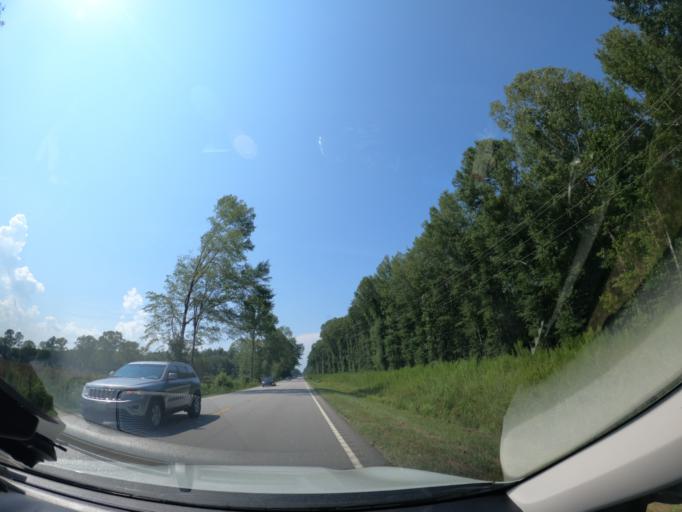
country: US
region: South Carolina
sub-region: Richland County
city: Hopkins
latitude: 33.8822
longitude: -80.9053
